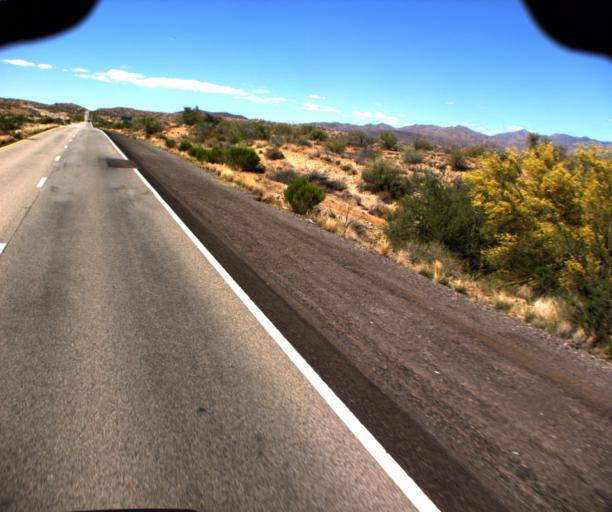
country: US
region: Arizona
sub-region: Mohave County
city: Kingman
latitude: 34.8886
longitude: -113.6507
